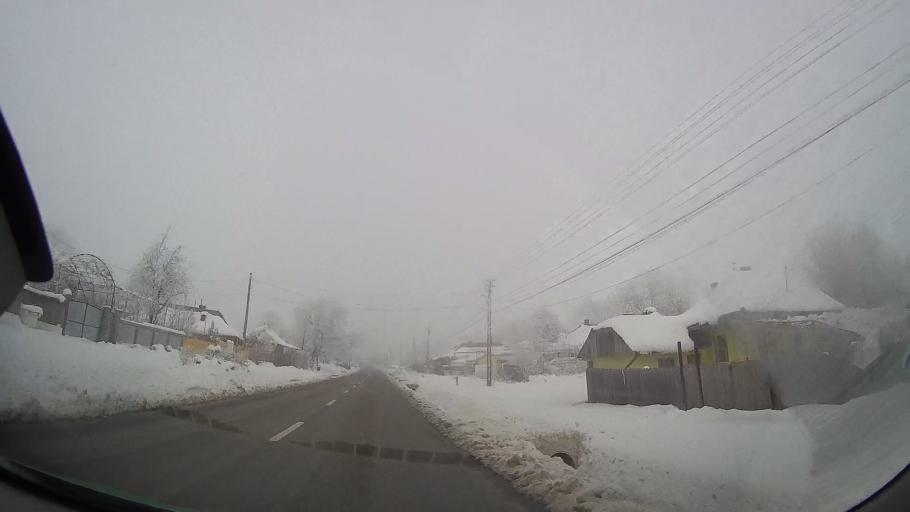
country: RO
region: Iasi
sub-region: Comuna Halaucesti
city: Halaucesti
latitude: 47.0971
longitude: 26.8189
